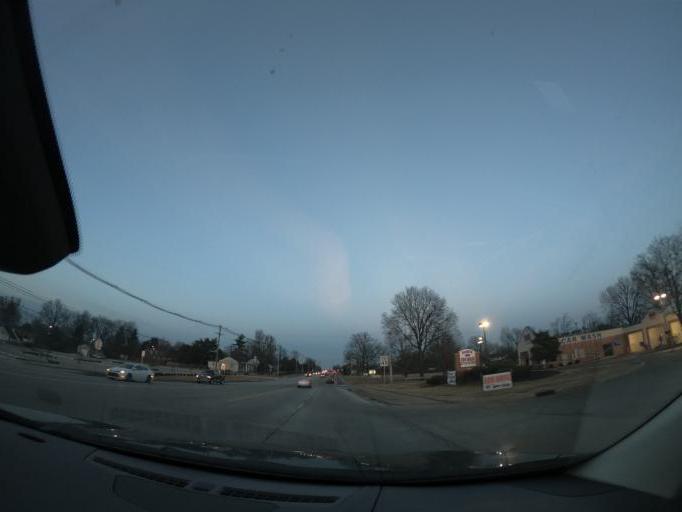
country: US
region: Kentucky
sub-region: Jefferson County
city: Worthington
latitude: 38.2880
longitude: -85.5712
